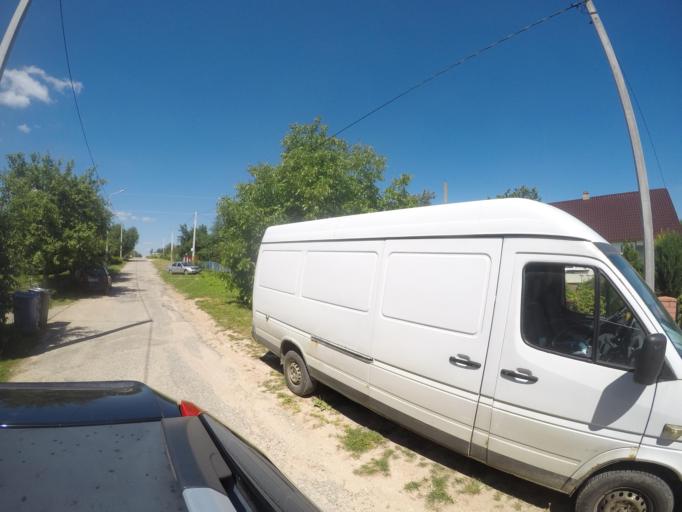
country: BY
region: Grodnenskaya
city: Hrodna
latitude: 53.7199
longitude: 23.8545
